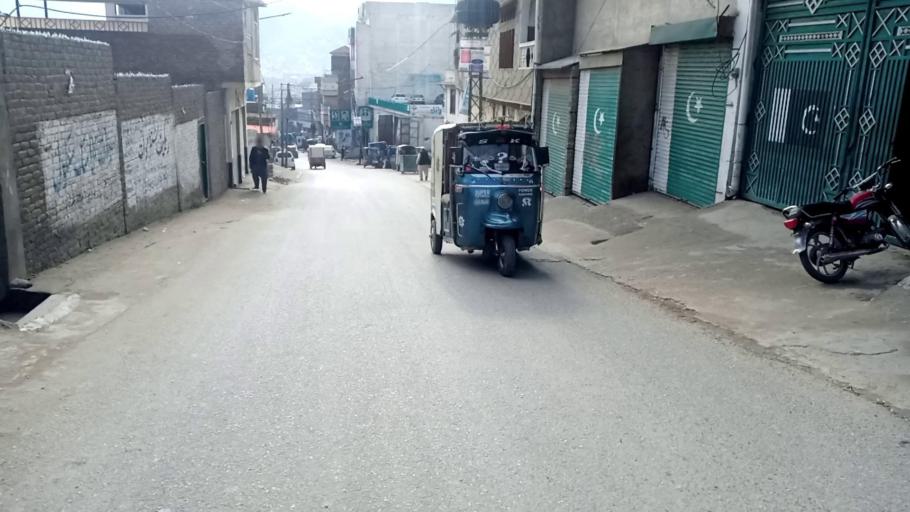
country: PK
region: Khyber Pakhtunkhwa
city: Mingora
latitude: 34.7735
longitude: 72.3674
